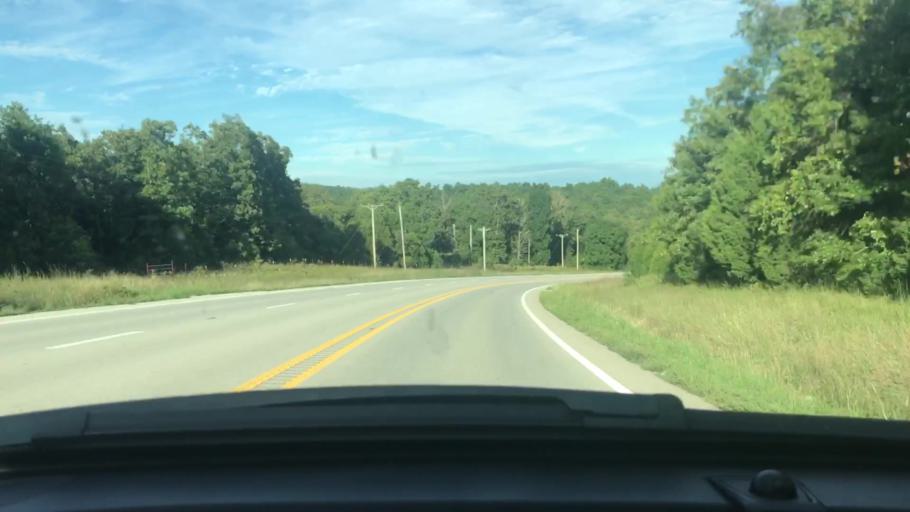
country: US
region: Arkansas
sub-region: Sharp County
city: Cherokee Village
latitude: 36.2746
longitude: -91.3623
